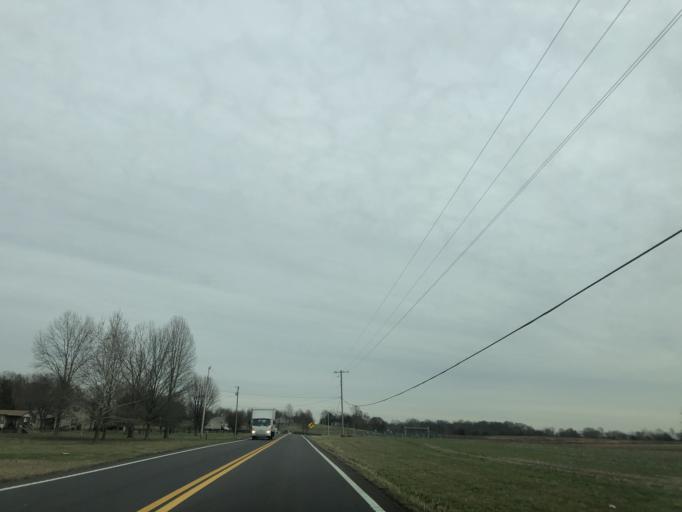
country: US
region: Tennessee
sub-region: Sumner County
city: White House
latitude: 36.4765
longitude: -86.7217
